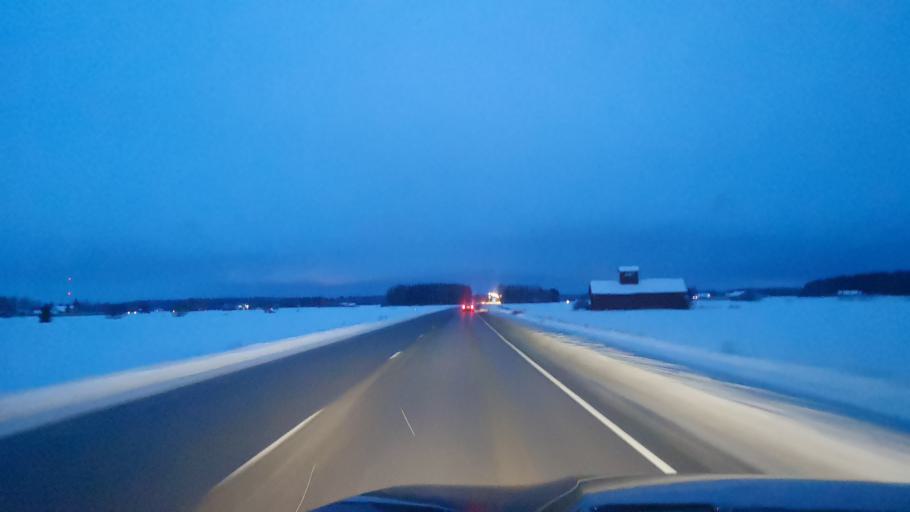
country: FI
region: Varsinais-Suomi
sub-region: Loimaa
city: Loimaa
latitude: 60.8787
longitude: 23.0752
